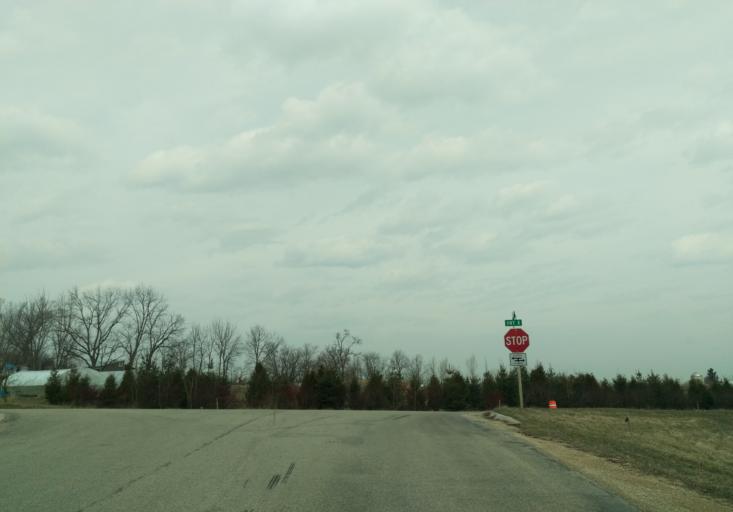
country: US
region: Wisconsin
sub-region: Dane County
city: Middleton
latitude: 43.1412
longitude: -89.4919
